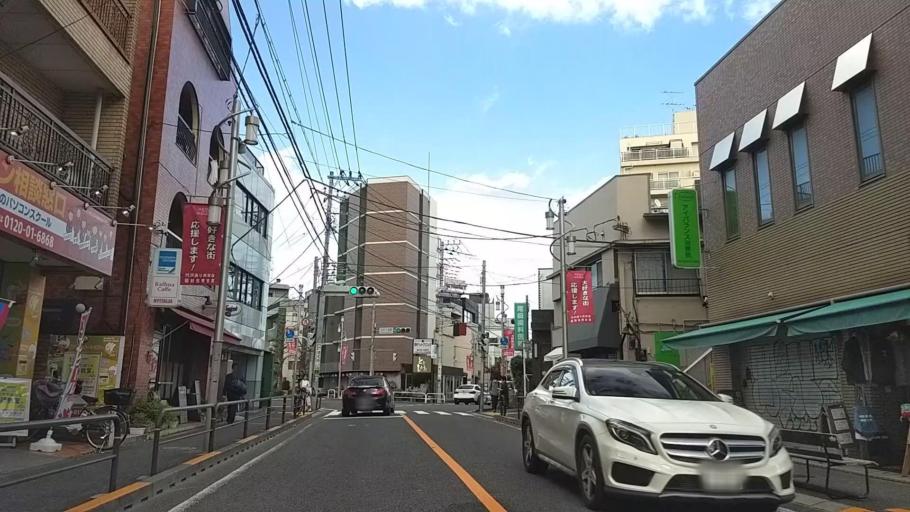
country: JP
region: Tokyo
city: Tokyo
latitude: 35.6573
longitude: 139.6677
